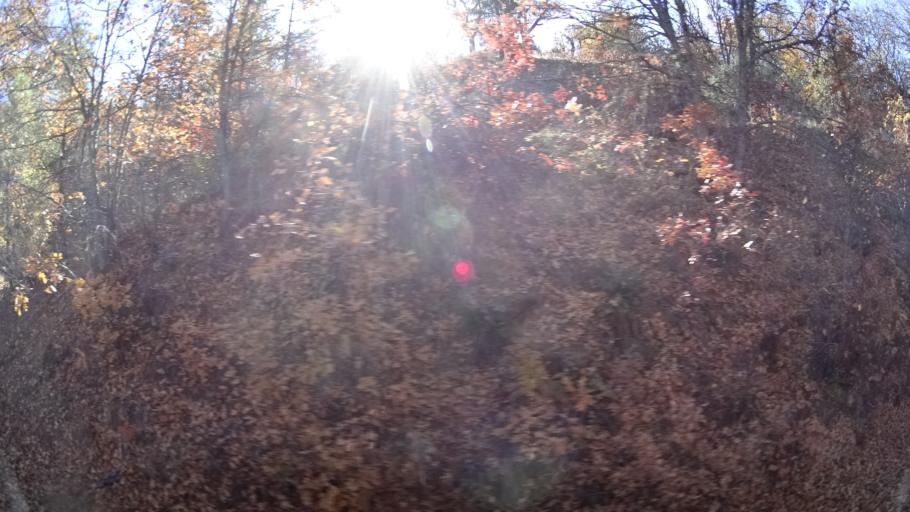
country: US
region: California
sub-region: Siskiyou County
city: Yreka
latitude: 41.8417
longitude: -122.8884
